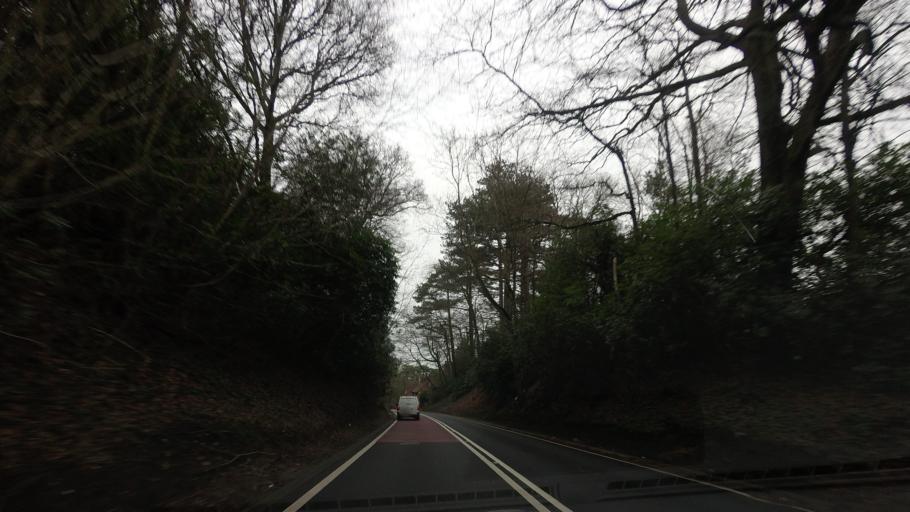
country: GB
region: England
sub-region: East Sussex
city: Saint Leonards-on-Sea
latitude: 50.8975
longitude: 0.5557
